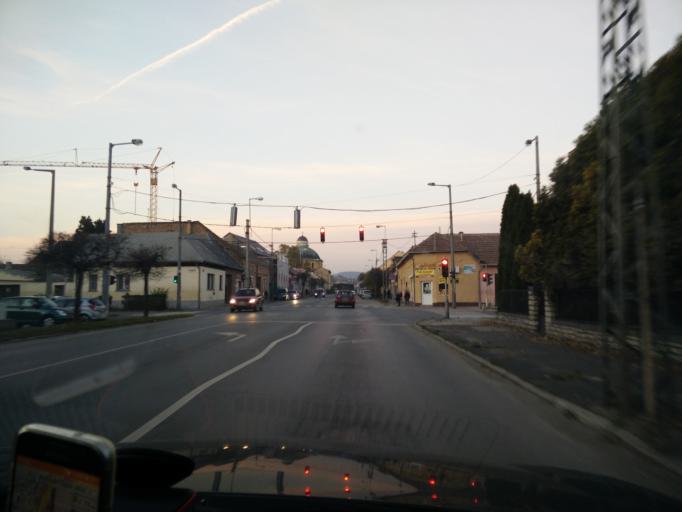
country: HU
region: Komarom-Esztergom
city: Esztergom
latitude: 47.7815
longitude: 18.7396
